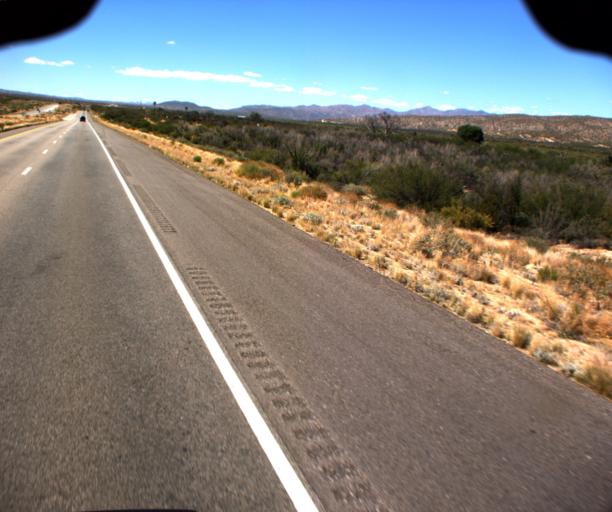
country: US
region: Arizona
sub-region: Yavapai County
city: Bagdad
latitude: 34.8273
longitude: -113.6288
